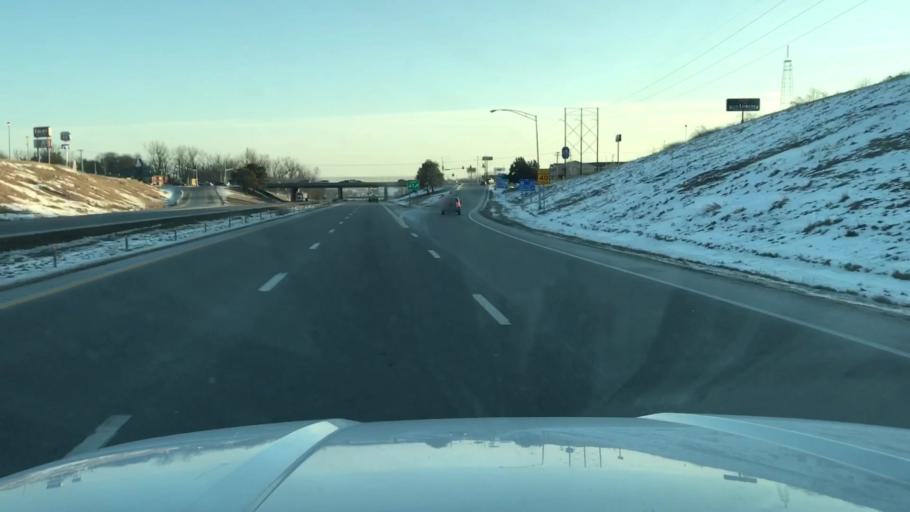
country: US
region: Missouri
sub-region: Buchanan County
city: Saint Joseph
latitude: 39.7799
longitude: -94.7943
